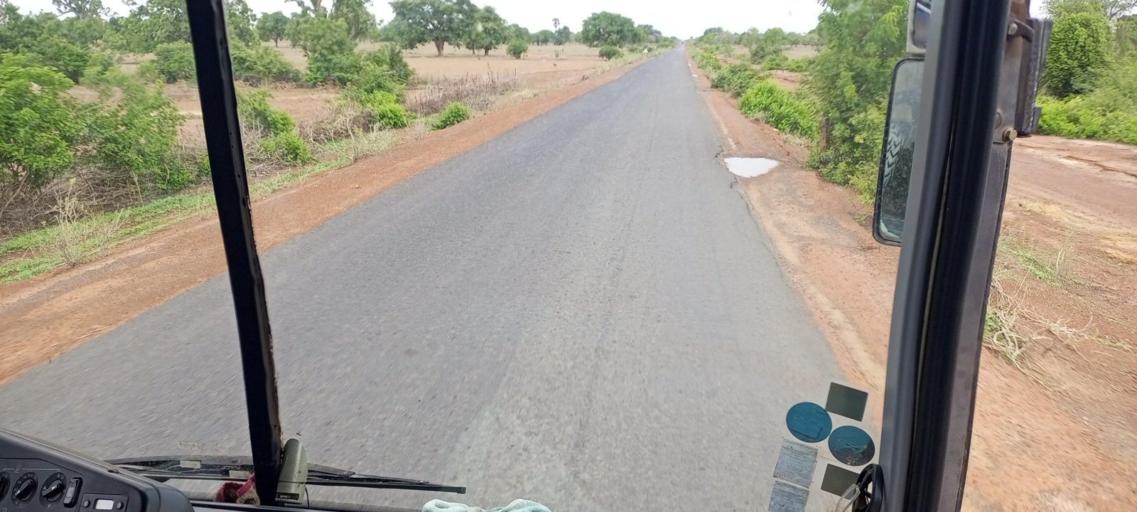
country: ML
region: Segou
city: Bla
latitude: 12.7315
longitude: -5.7255
